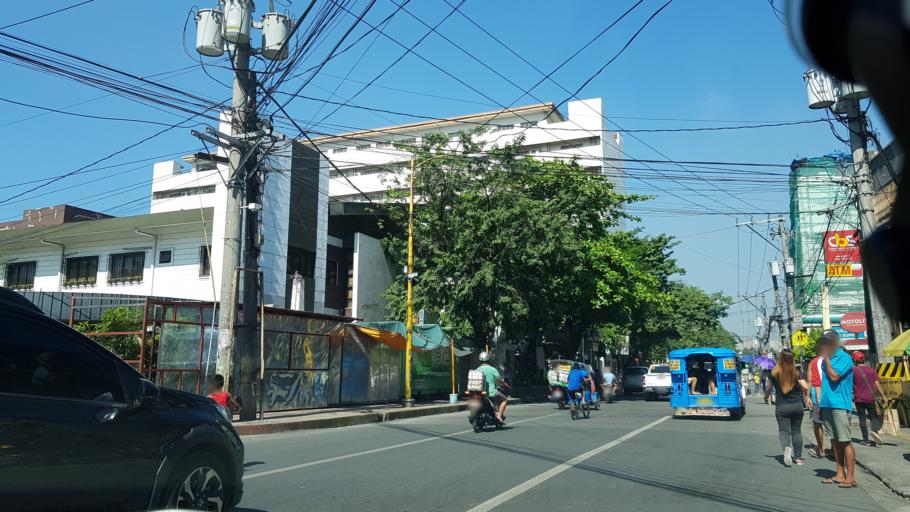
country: PH
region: Calabarzon
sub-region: Province of Rizal
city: Pateros
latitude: 14.5597
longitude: 121.0836
